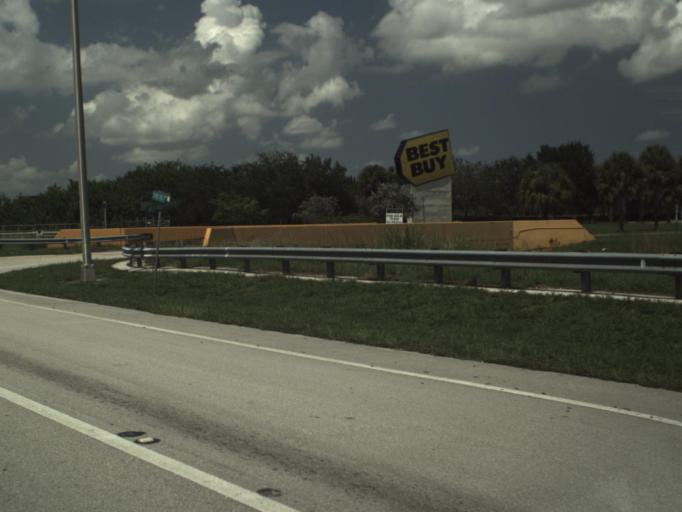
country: US
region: Florida
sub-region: Palm Beach County
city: Boca Pointe
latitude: 26.3706
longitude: -80.2034
